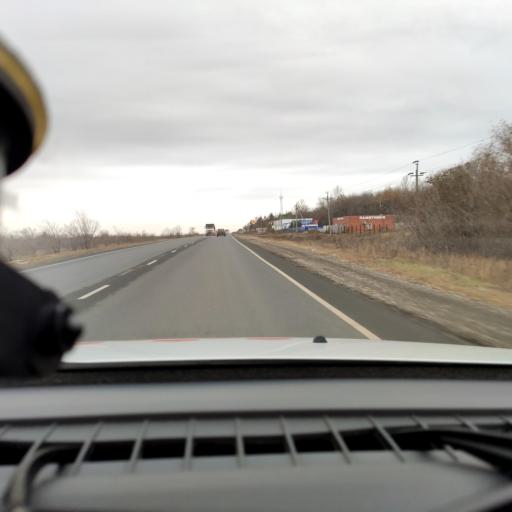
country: RU
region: Samara
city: Samara
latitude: 53.1237
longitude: 50.1902
